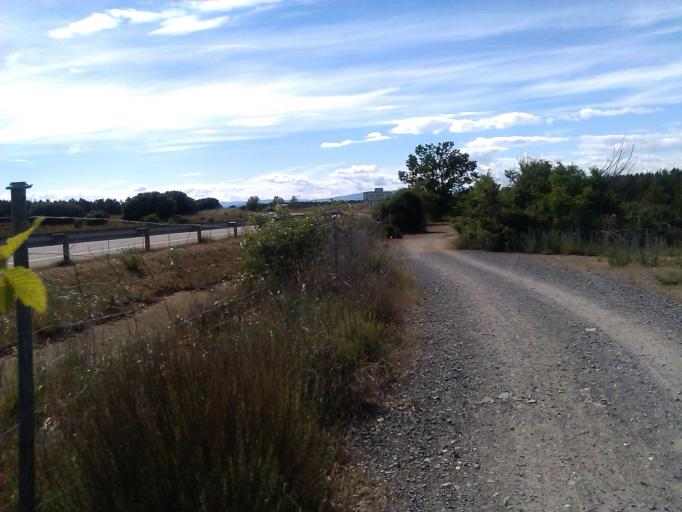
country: ES
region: Castille and Leon
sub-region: Provincia de Leon
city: San Justo de la Vega
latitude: 42.4525
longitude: -5.9875
